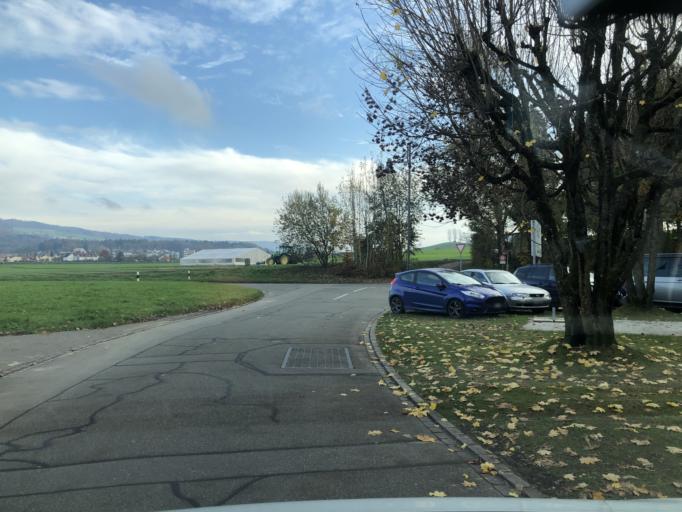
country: CH
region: Aargau
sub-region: Bezirk Baden
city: Mellingen
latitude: 47.4402
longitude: 8.2753
